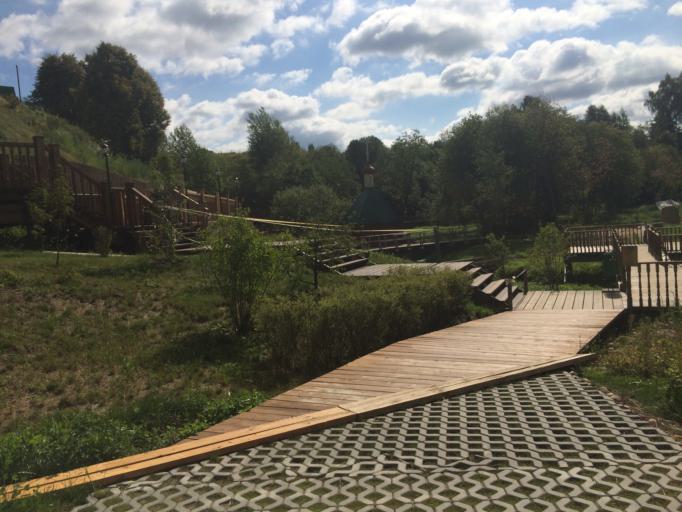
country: RU
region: Moskovskaya
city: Khot'kovo
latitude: 56.2079
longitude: 38.0380
